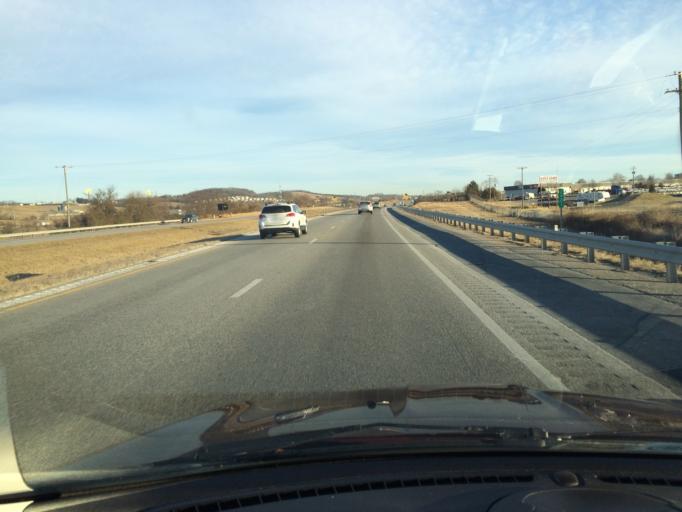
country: US
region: Virginia
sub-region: Rockingham County
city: Dayton
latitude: 38.3850
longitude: -78.9161
